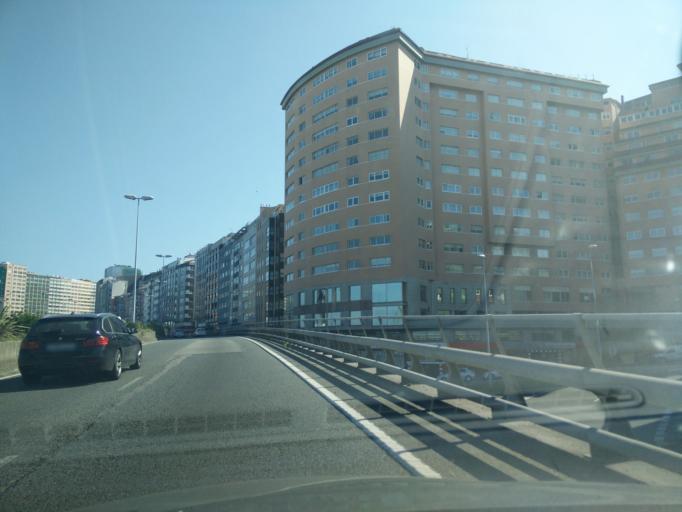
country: ES
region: Galicia
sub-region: Provincia da Coruna
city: A Coruna
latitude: 43.3552
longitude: -8.3964
